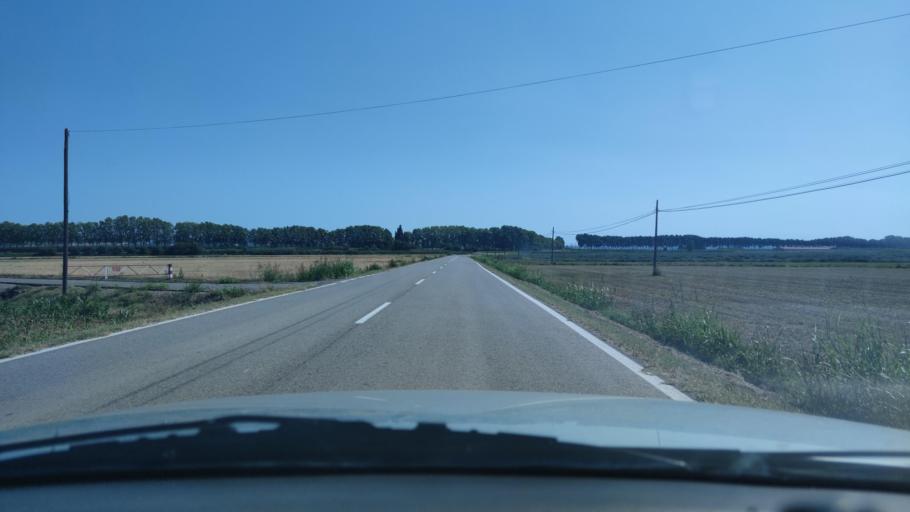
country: ES
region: Catalonia
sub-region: Provincia de Lleida
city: Linyola
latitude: 41.7245
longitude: 0.9213
